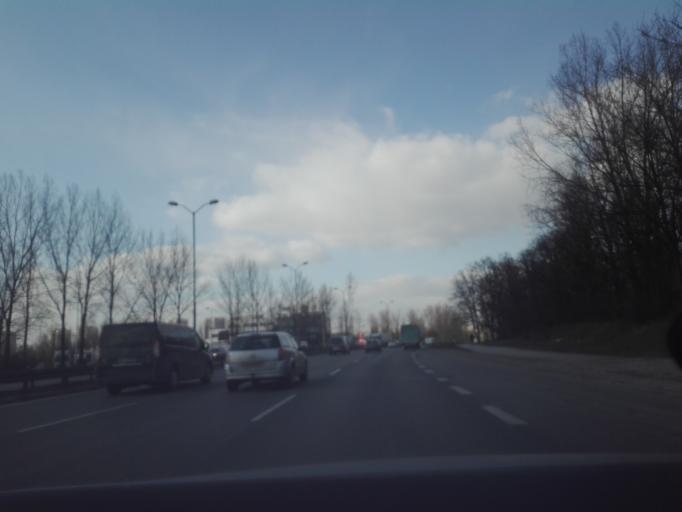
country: PL
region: Silesian Voivodeship
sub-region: Katowice
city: Katowice
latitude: 50.2532
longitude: 19.0481
